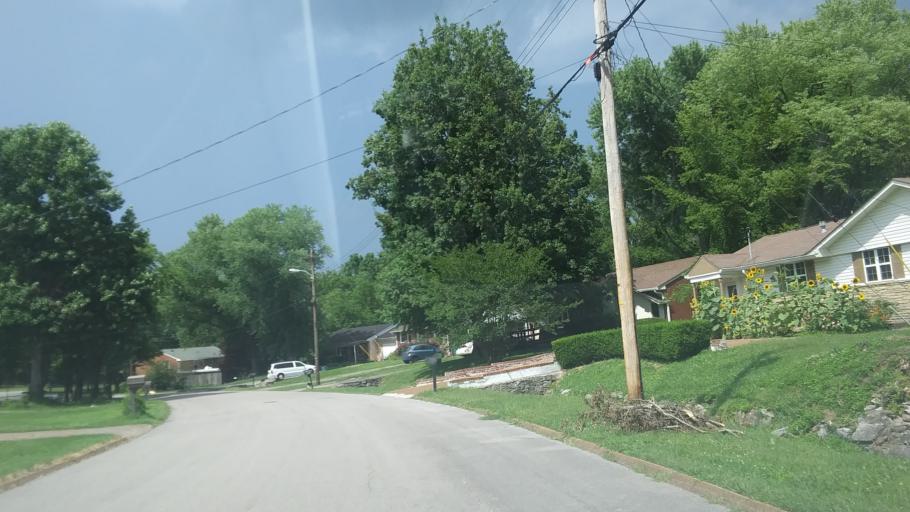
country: US
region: Tennessee
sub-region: Davidson County
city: Oak Hill
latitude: 36.0778
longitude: -86.7050
